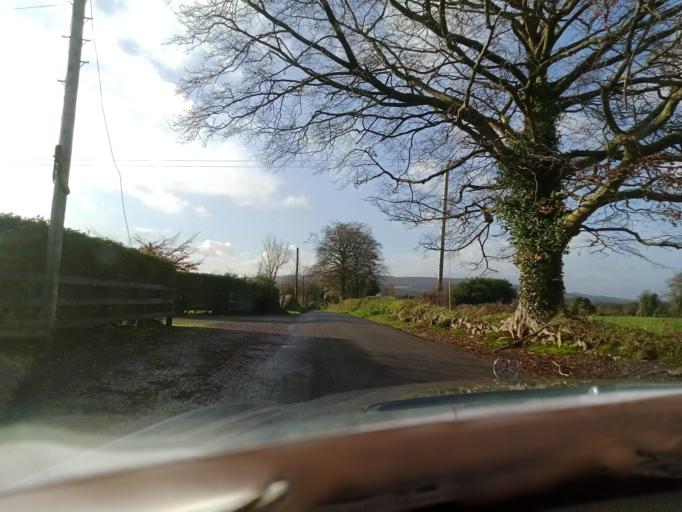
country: IE
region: Leinster
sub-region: Kilkenny
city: Mooncoin
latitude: 52.3322
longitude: -7.2719
